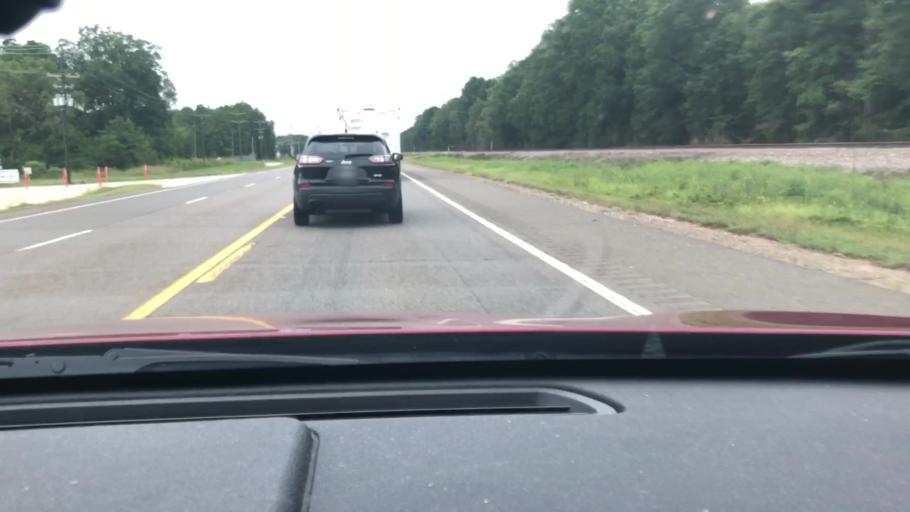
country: US
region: Arkansas
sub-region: Lafayette County
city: Lewisville
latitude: 33.3580
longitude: -93.6042
